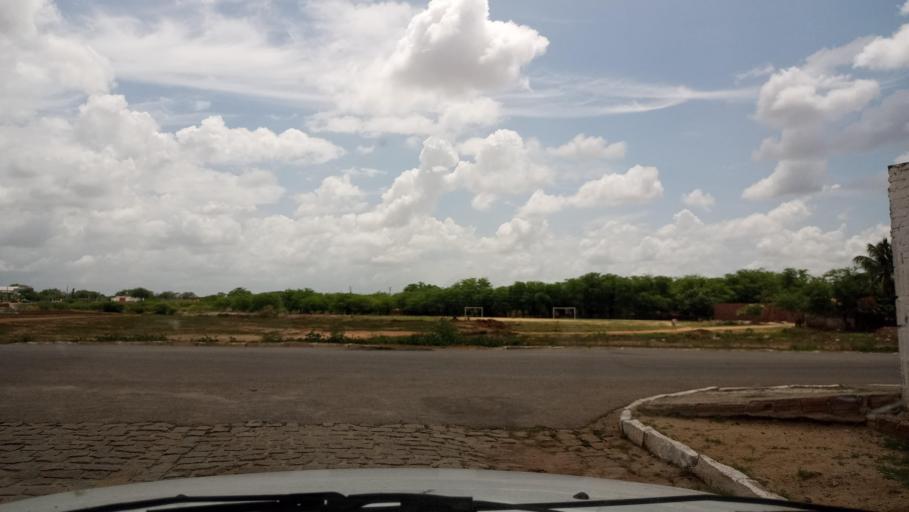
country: BR
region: Rio Grande do Norte
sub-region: Tangara
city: Tangara
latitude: -6.1093
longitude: -35.7142
